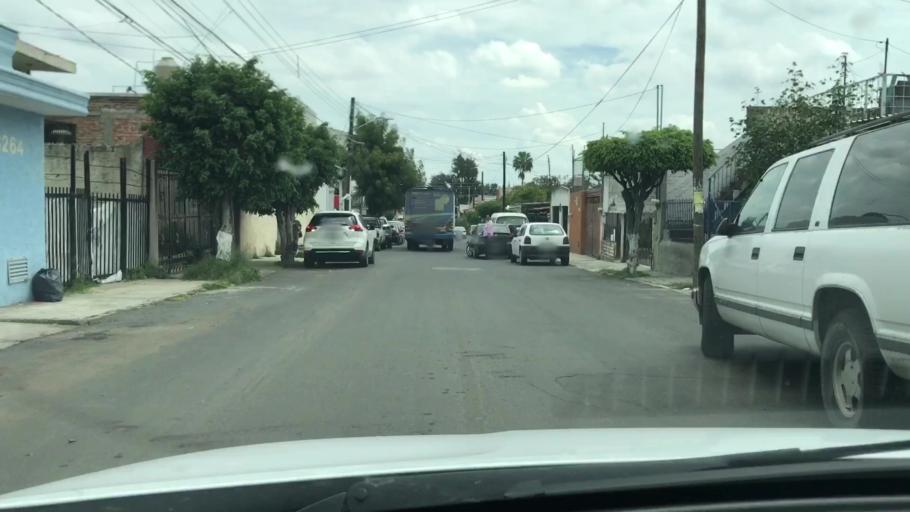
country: MX
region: Jalisco
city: Guadalajara
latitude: 20.6444
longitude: -103.4362
